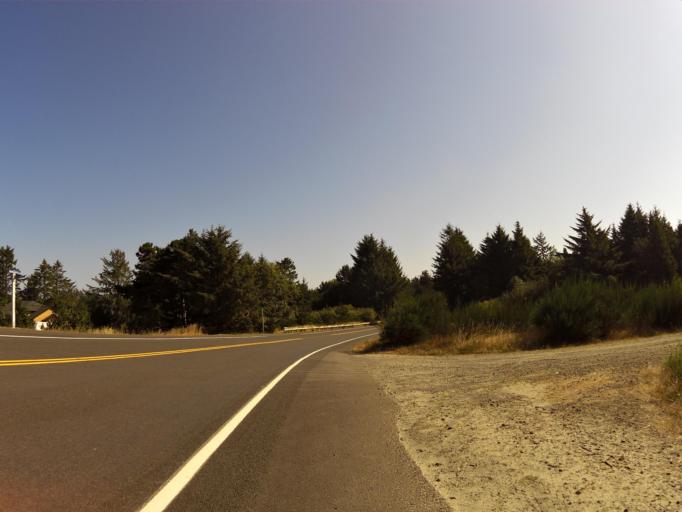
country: US
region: Oregon
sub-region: Clatsop County
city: Gearhart
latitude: 46.0495
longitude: -123.9212
